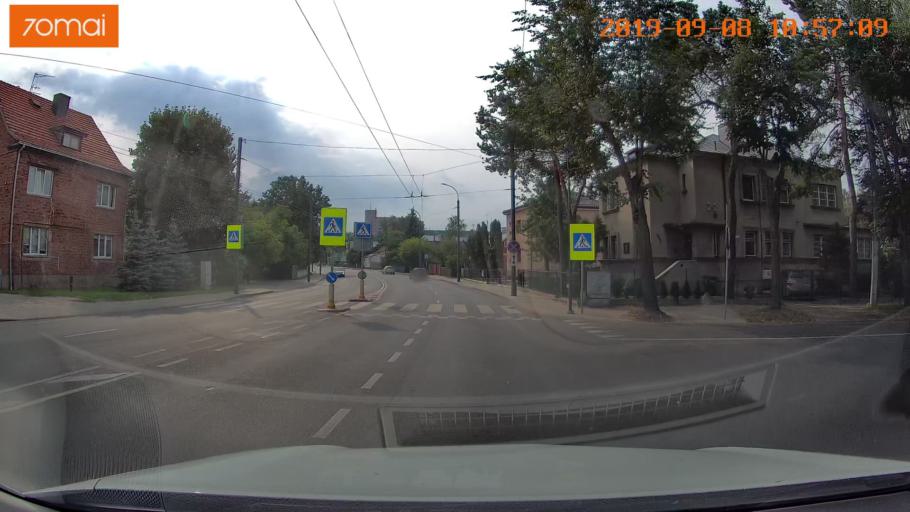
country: LT
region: Kauno apskritis
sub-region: Kaunas
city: Eiguliai
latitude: 54.9117
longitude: 23.9251
